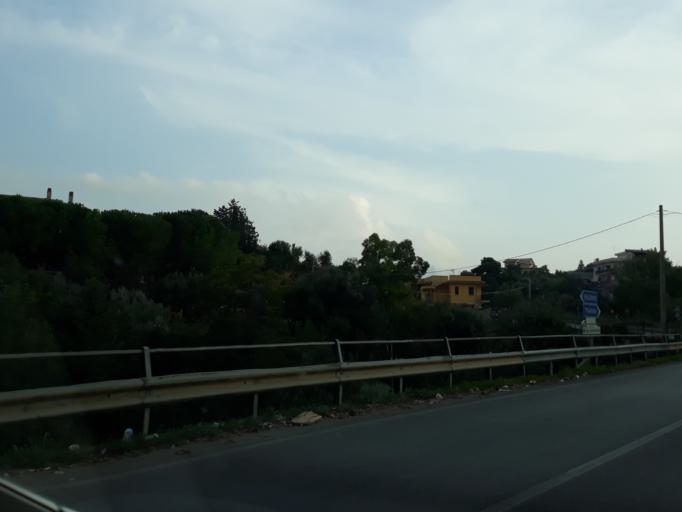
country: IT
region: Sicily
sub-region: Palermo
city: Cannizzaro-Favara
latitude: 38.0703
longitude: 13.2694
